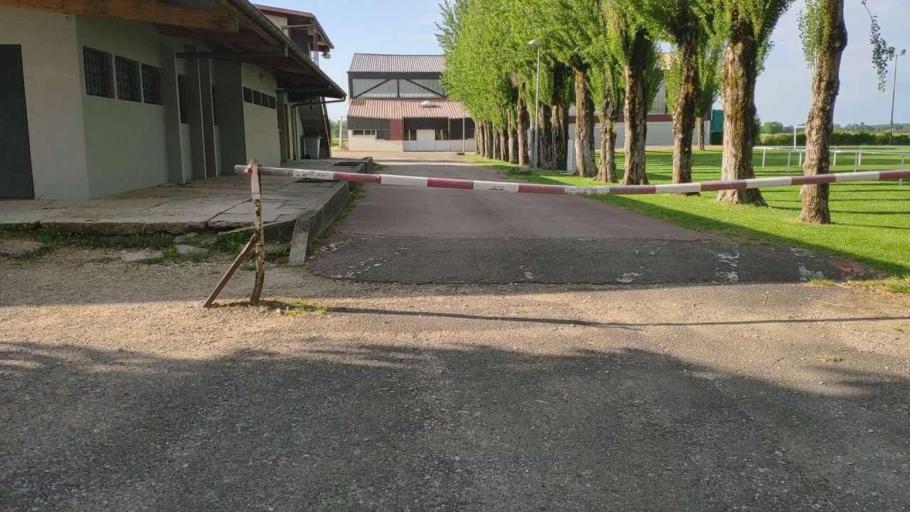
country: FR
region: Franche-Comte
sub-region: Departement du Jura
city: Bletterans
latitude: 46.7434
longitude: 5.4539
